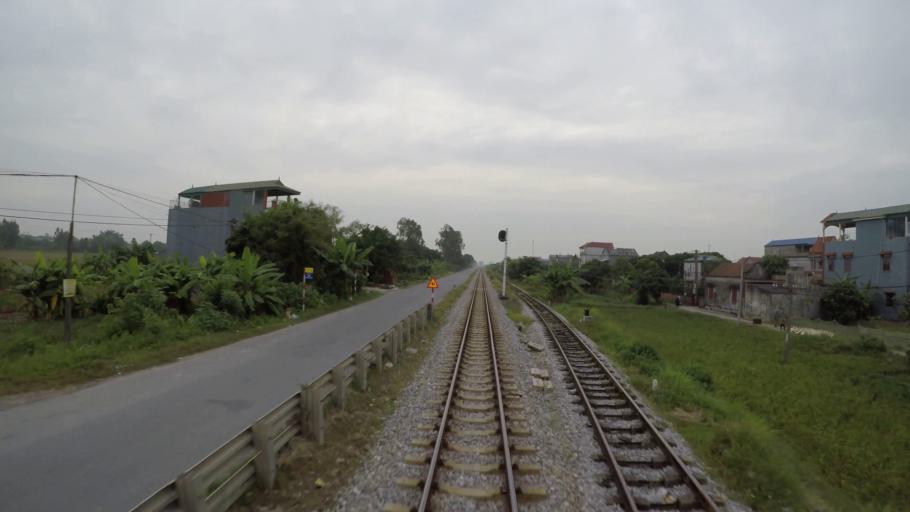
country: VN
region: Hung Yen
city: Ban Yen Nhan
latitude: 20.9735
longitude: 106.0945
